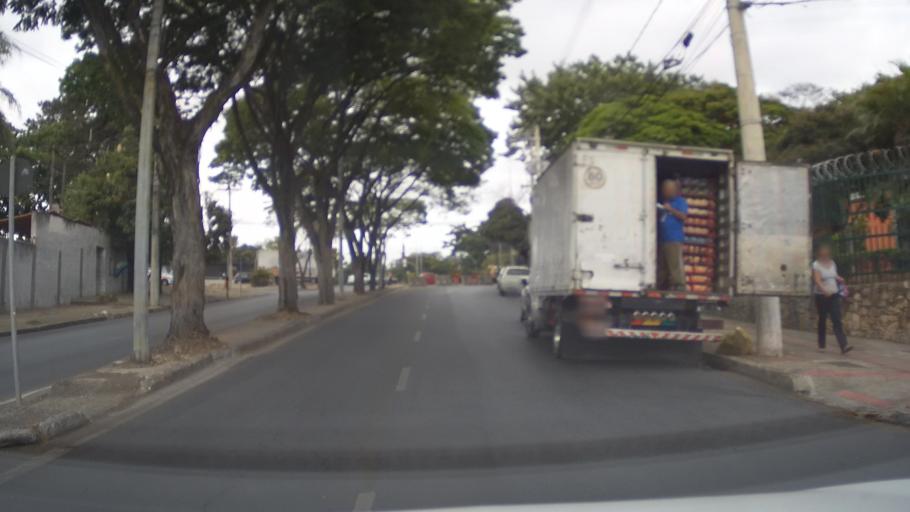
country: BR
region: Minas Gerais
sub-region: Belo Horizonte
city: Belo Horizonte
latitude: -19.8521
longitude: -43.9611
